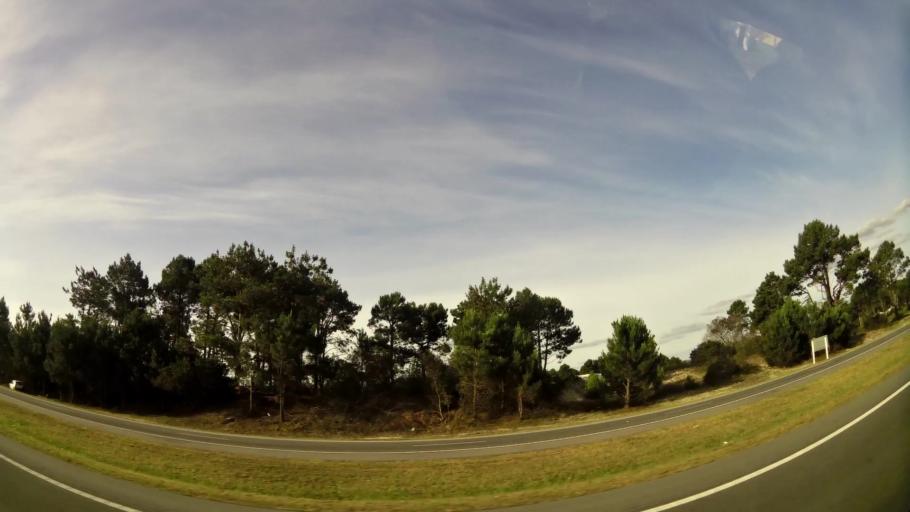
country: UY
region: Maldonado
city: Piriapolis
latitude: -34.7804
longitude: -55.4192
